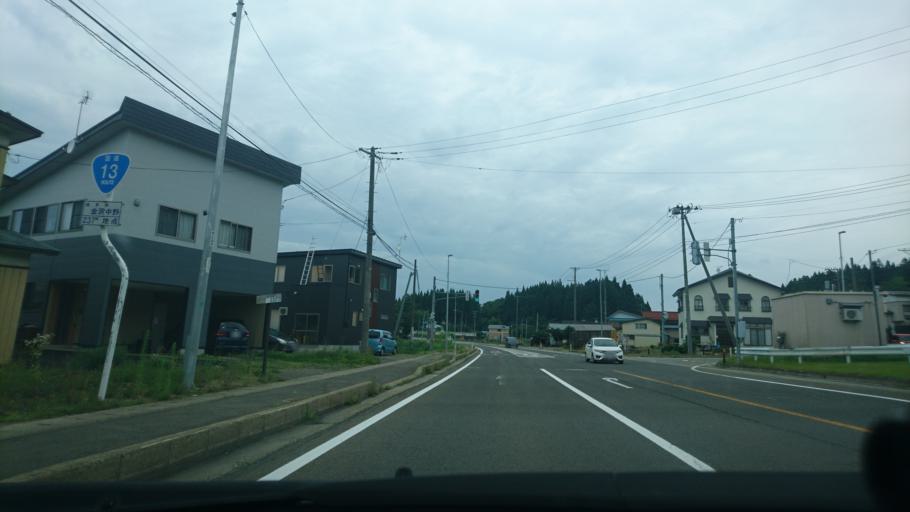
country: JP
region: Akita
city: Yokotemachi
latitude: 39.3715
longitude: 140.5690
